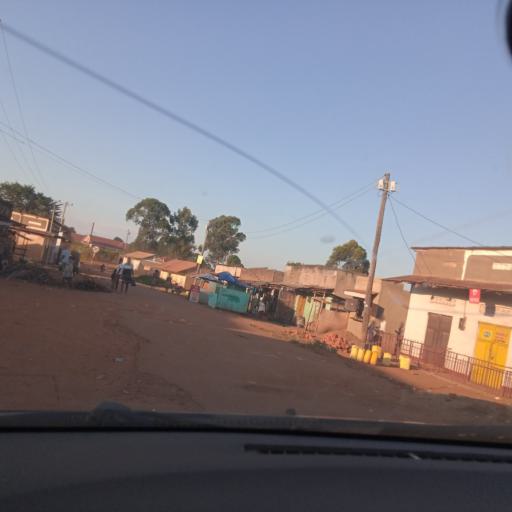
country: UG
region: Central Region
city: Masaka
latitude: -0.3428
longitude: 31.7602
